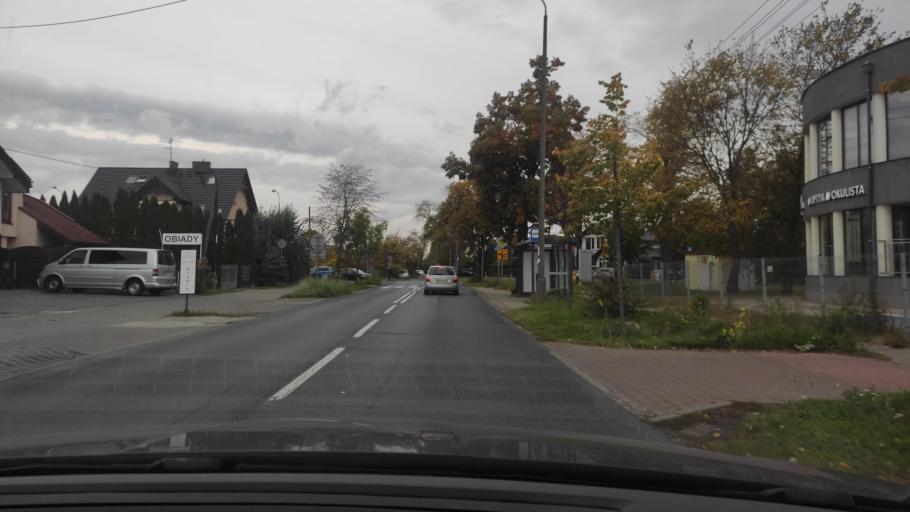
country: PL
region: Greater Poland Voivodeship
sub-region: Poznan
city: Poznan
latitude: 52.3712
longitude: 16.9959
